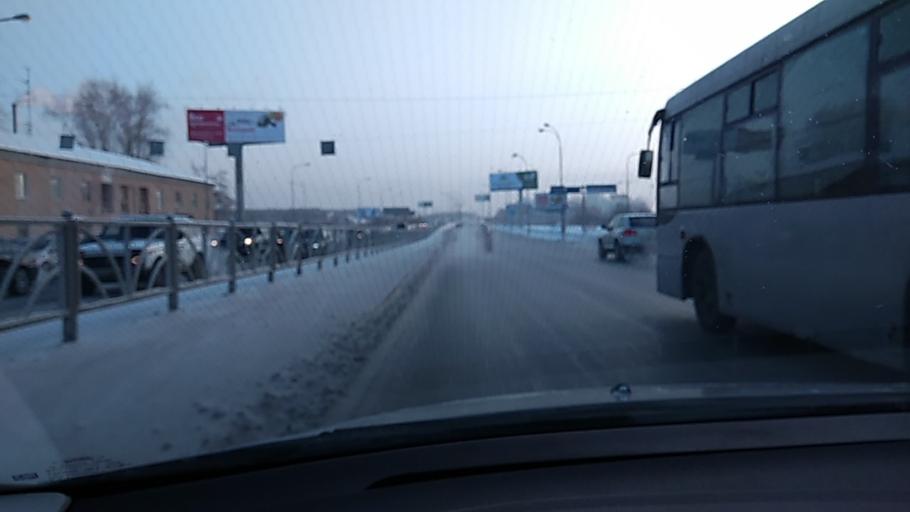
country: RU
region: Sverdlovsk
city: Yekaterinburg
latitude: 56.8017
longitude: 60.6378
